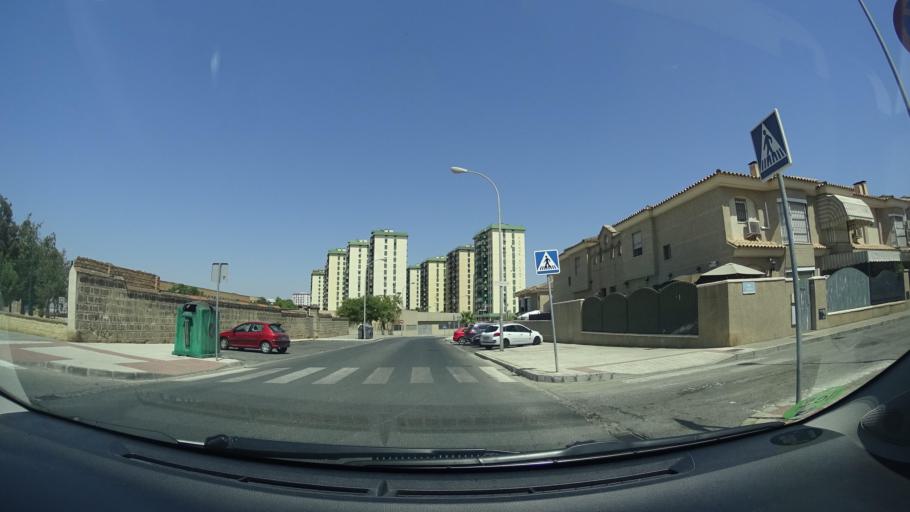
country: ES
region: Andalusia
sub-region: Provincia de Cadiz
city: Jerez de la Frontera
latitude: 36.6768
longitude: -6.1239
